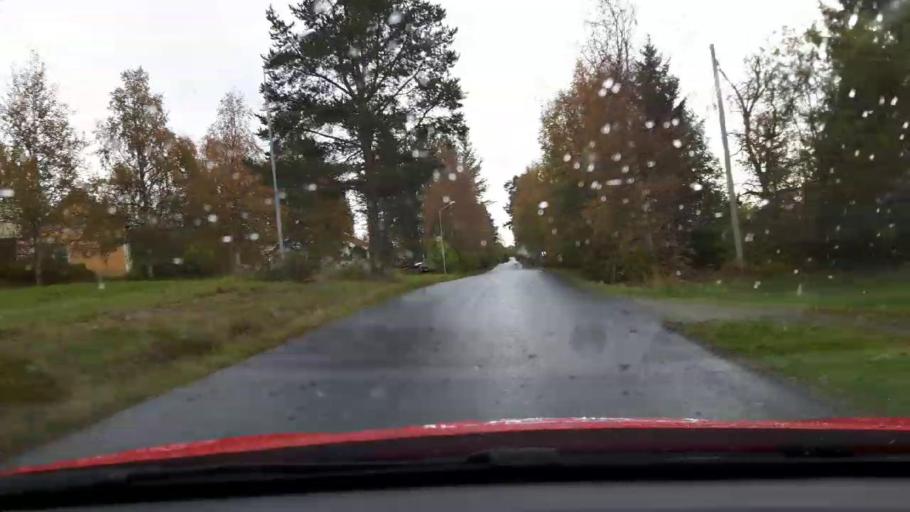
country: SE
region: Jaemtland
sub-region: Bergs Kommun
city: Hoverberg
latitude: 62.9310
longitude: 14.5158
